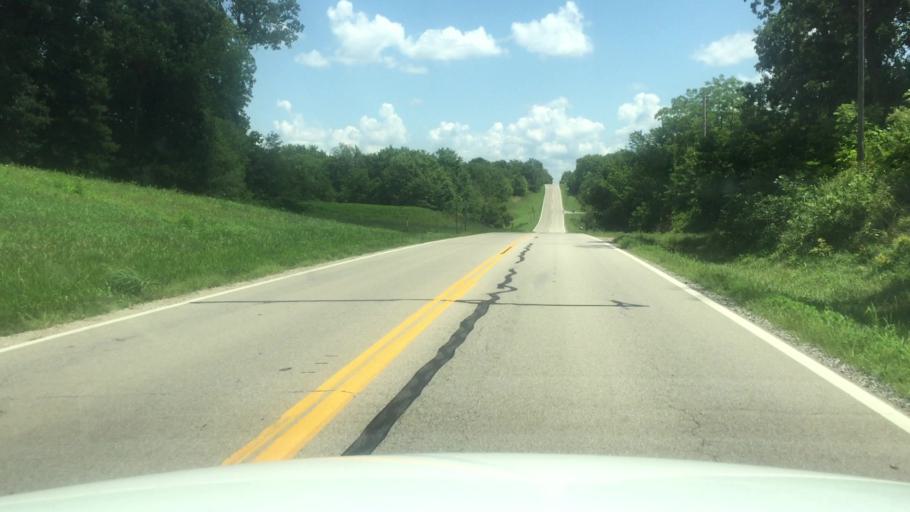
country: US
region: Kansas
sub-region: Brown County
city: Horton
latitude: 39.6673
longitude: -95.5415
